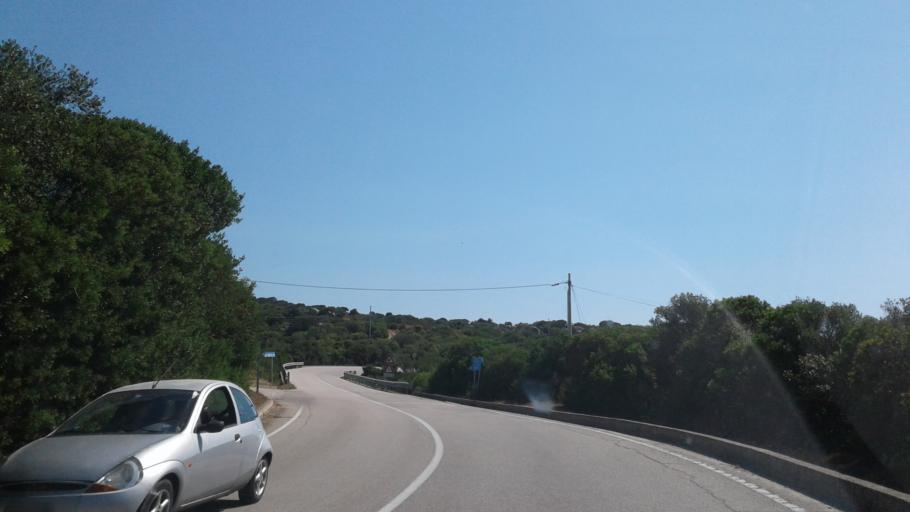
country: IT
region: Sardinia
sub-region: Provincia di Olbia-Tempio
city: Palau
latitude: 41.1287
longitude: 9.2868
